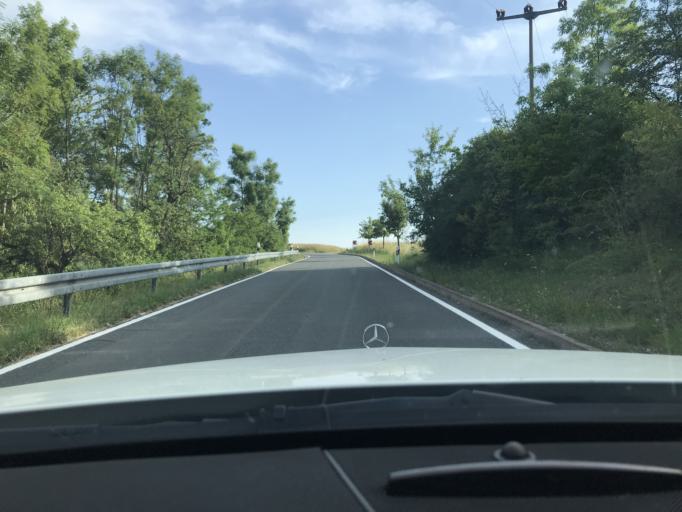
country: DE
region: Thuringia
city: Katharinenberg
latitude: 51.1888
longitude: 10.2532
